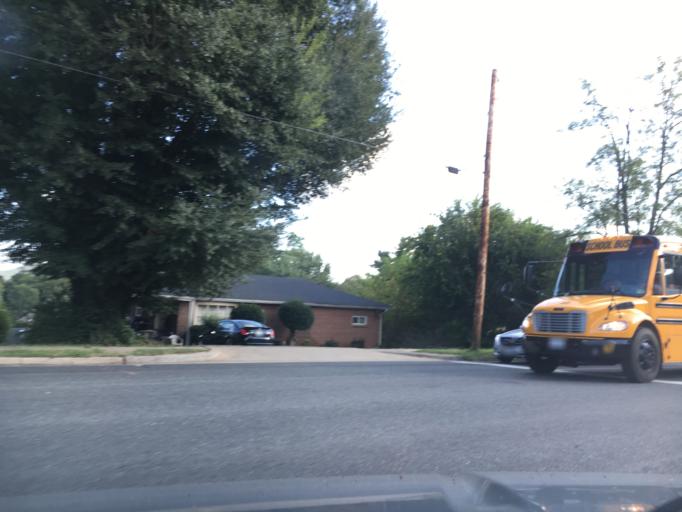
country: US
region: Virginia
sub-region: City of Lynchburg
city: West Lynchburg
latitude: 37.3839
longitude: -79.1791
